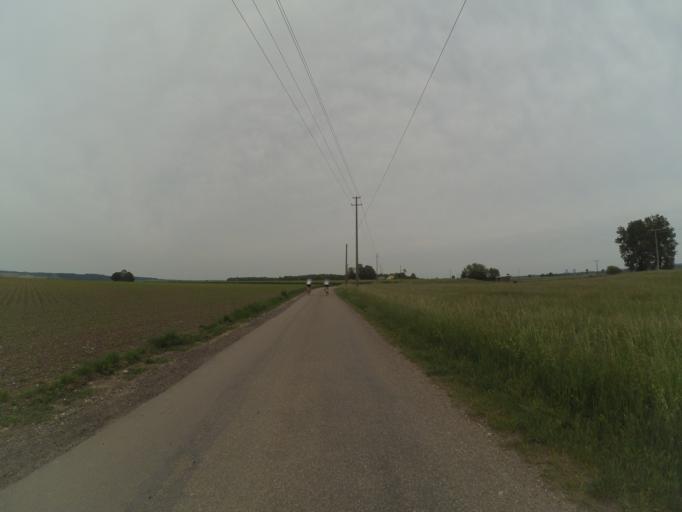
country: DE
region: Baden-Wuerttemberg
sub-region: Regierungsbezirk Stuttgart
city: Niederstotzingen
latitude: 48.5119
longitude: 10.2622
